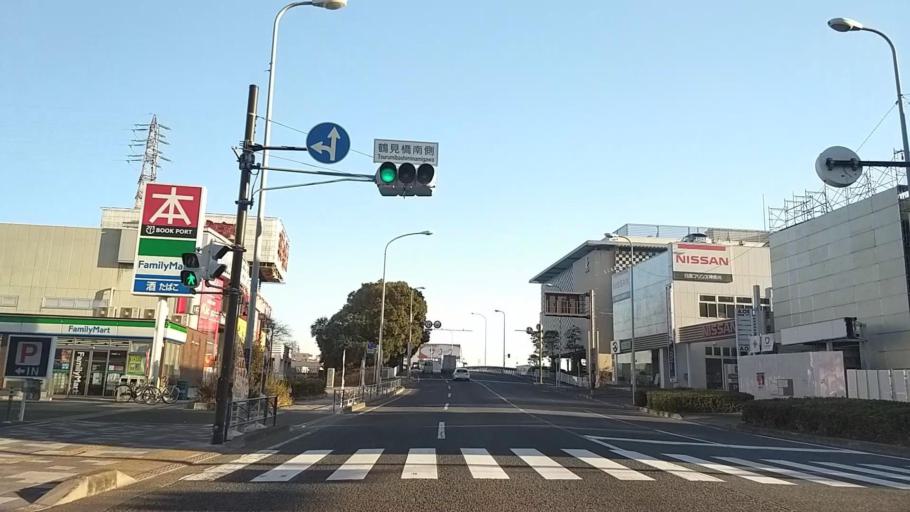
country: JP
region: Kanagawa
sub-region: Kawasaki-shi
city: Kawasaki
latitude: 35.5114
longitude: 139.6841
